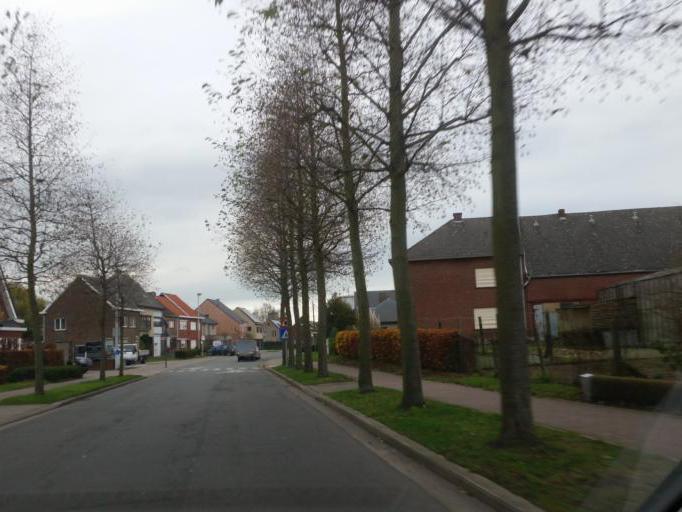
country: BE
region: Flanders
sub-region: Provincie Antwerpen
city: Duffel
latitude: 51.0706
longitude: 4.5054
